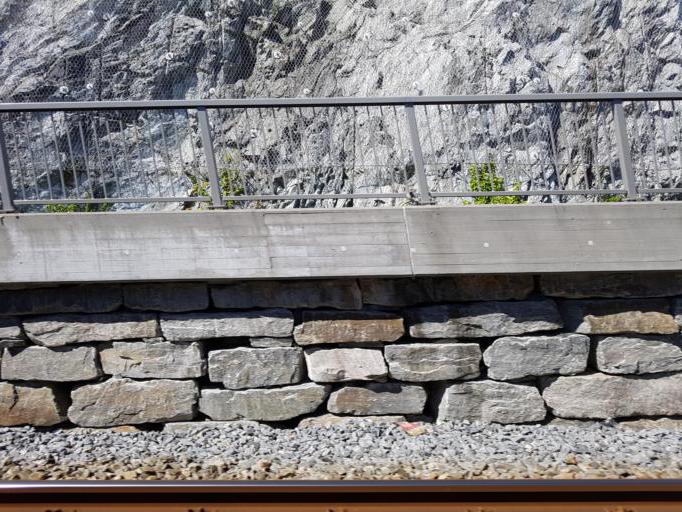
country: NO
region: Hordaland
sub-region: Bergen
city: Ytrebygda
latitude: 60.2947
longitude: 5.2684
